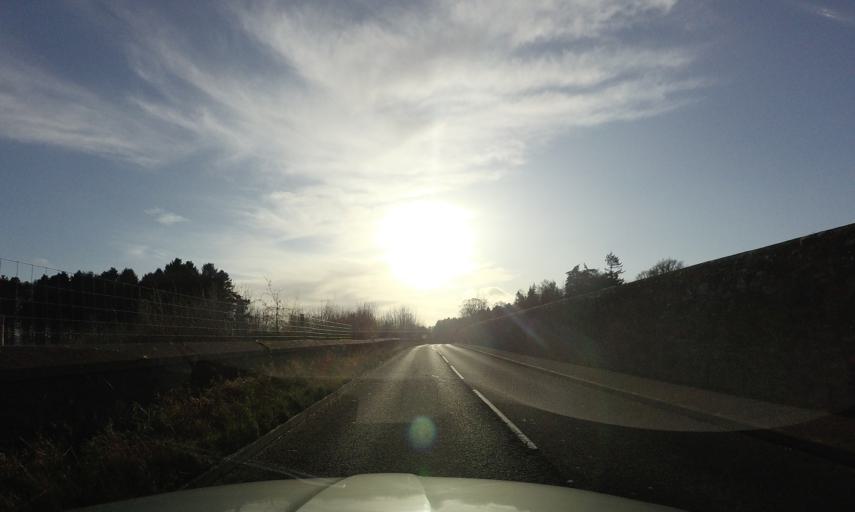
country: GB
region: Scotland
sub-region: Perth and Kinross
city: Errol
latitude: 56.3879
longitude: -3.2204
